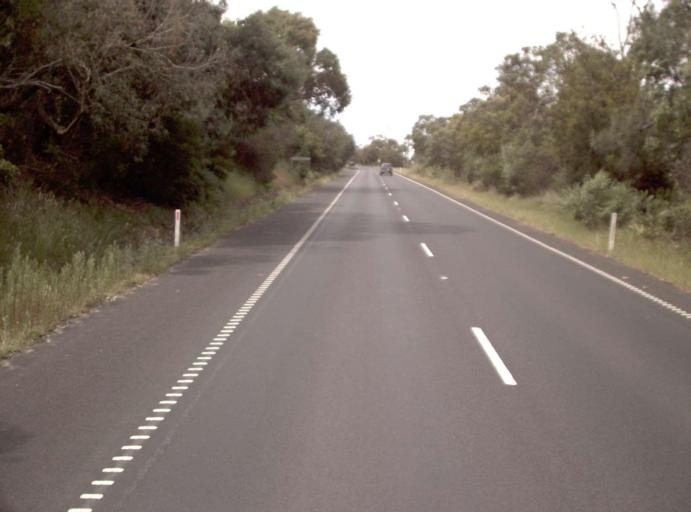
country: AU
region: Victoria
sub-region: Mornington Peninsula
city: Baxter
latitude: -38.1916
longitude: 145.1378
